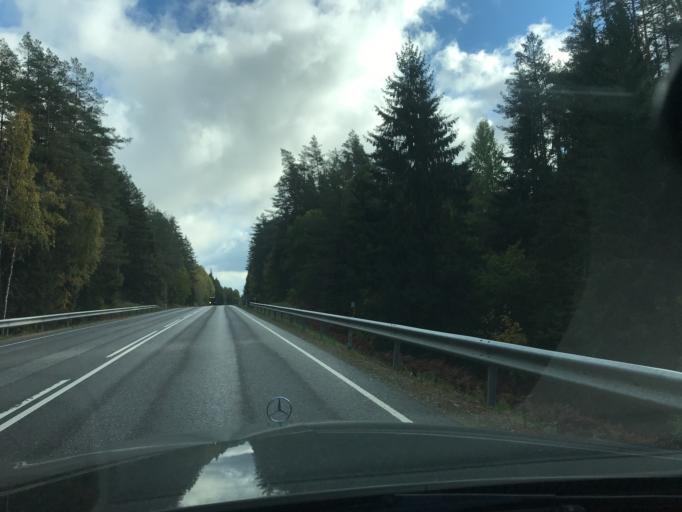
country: EE
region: Vorumaa
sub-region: Voru linn
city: Voru
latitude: 57.7661
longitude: 27.1822
